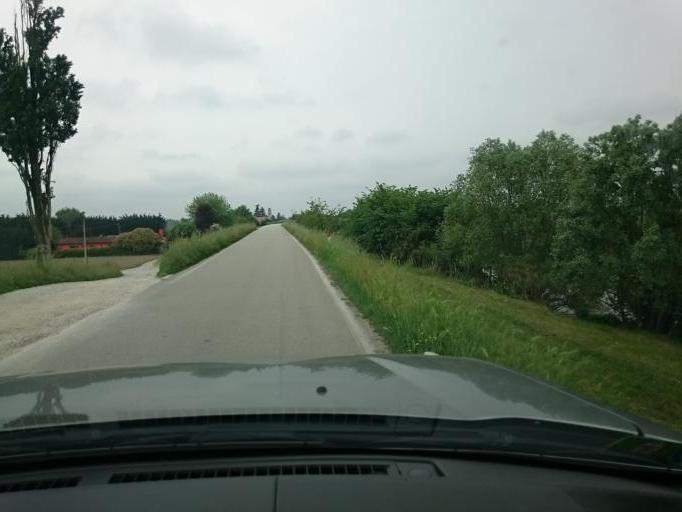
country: IT
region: Veneto
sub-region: Provincia di Padova
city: Campagnola
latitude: 45.2610
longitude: 11.9739
